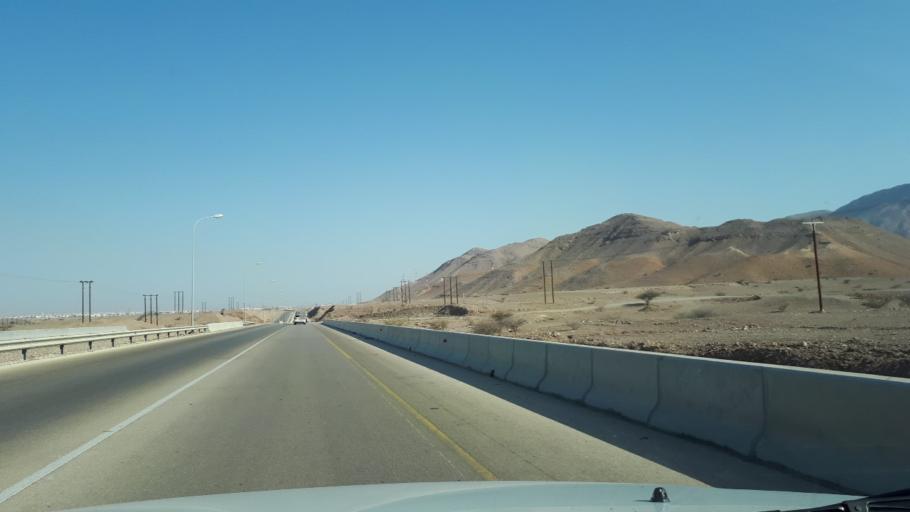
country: OM
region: Ash Sharqiyah
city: Sur
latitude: 22.6403
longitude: 59.4011
